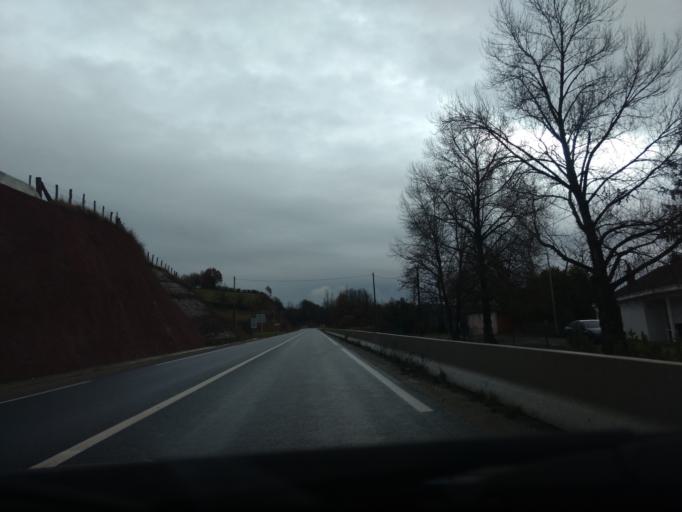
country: FR
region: Midi-Pyrenees
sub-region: Departement de l'Aveyron
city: Firmi
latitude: 44.5125
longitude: 2.3592
